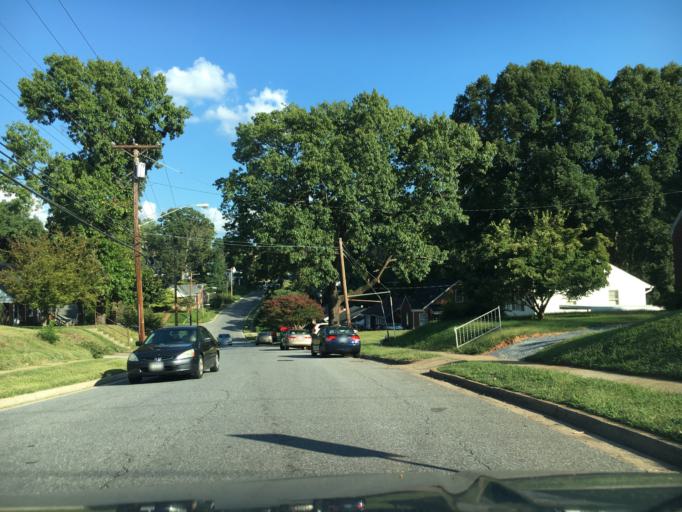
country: US
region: Virginia
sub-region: City of Lynchburg
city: West Lynchburg
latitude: 37.3863
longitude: -79.1832
